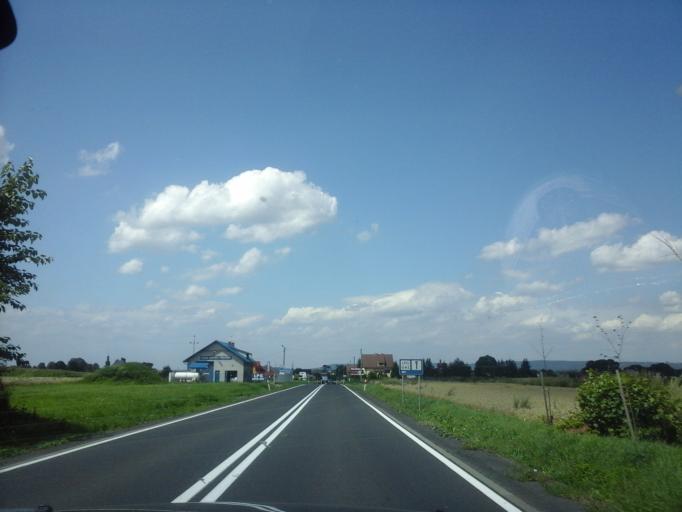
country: PL
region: Lesser Poland Voivodeship
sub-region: Powiat wadowicki
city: Spytkowice
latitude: 49.9917
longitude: 19.5193
